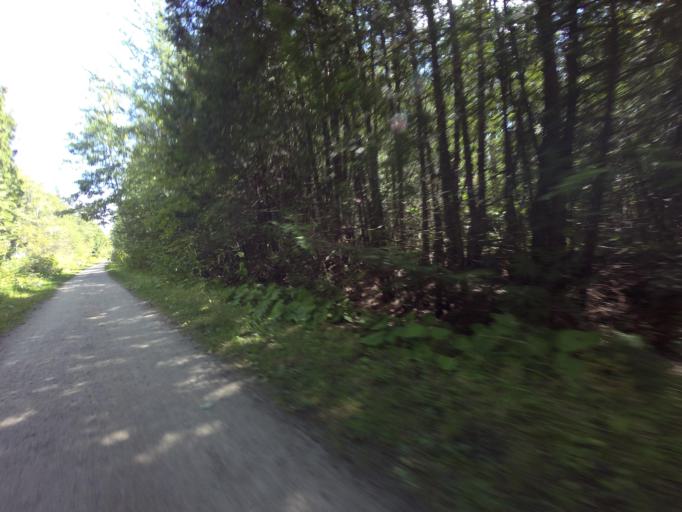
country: CA
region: Ontario
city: Orangeville
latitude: 43.7852
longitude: -80.1500
